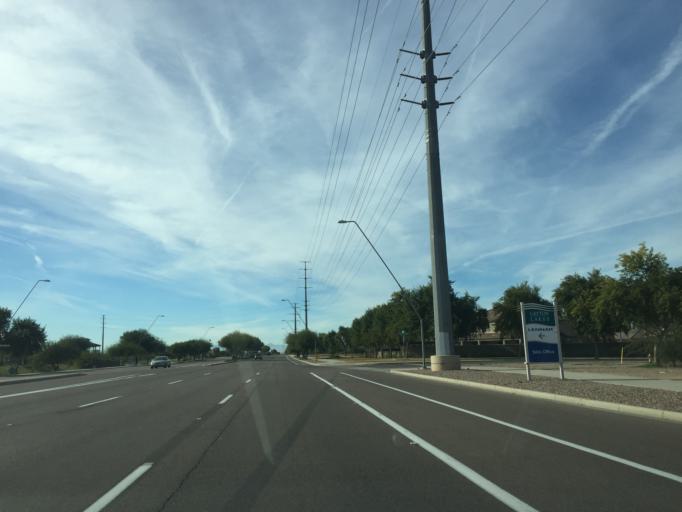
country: US
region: Arizona
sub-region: Maricopa County
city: Chandler
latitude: 33.2631
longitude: -111.7766
